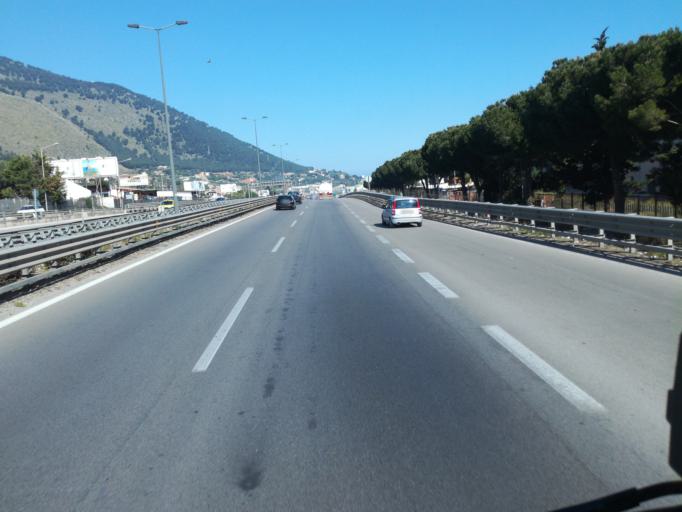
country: IT
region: Sicily
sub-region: Palermo
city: Palermo
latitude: 38.1693
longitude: 13.3013
